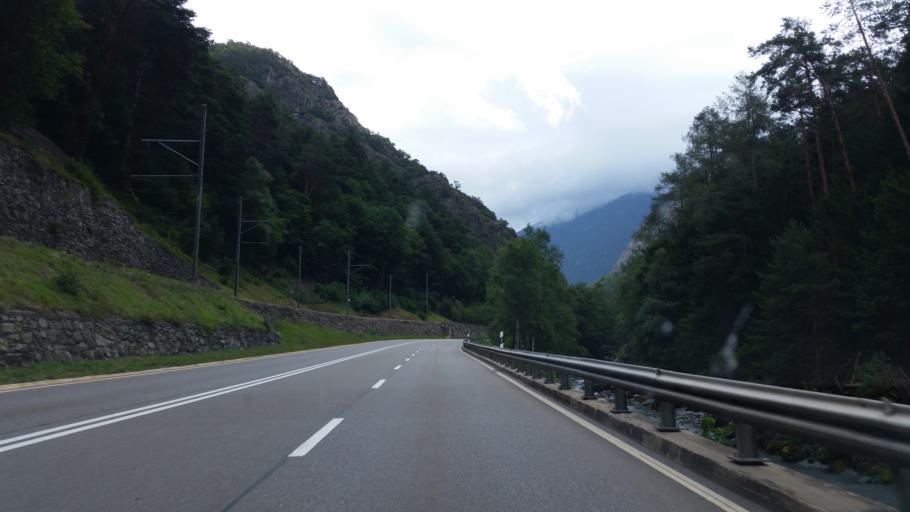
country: CH
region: Valais
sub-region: Martigny District
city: Charrat-les-Chenes
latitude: 46.0805
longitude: 7.1142
